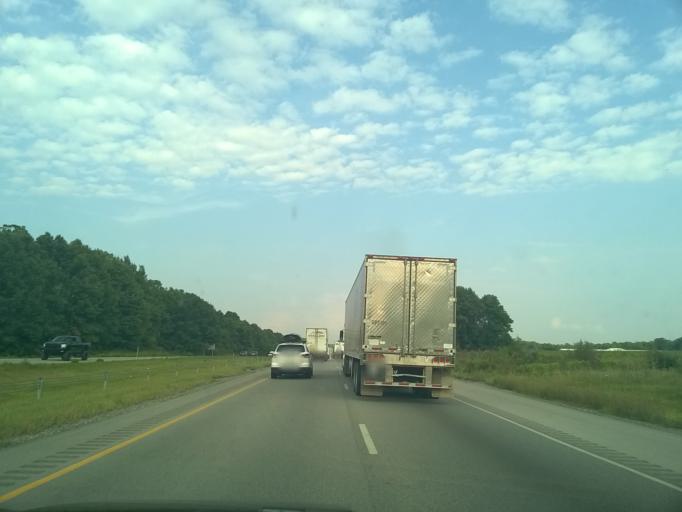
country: US
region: Indiana
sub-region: Putnam County
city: Cloverdale
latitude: 39.5331
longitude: -86.8471
